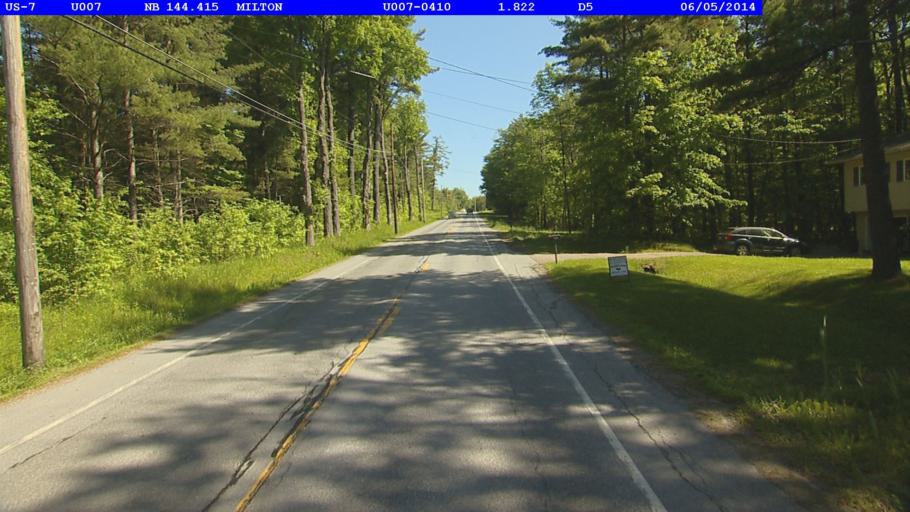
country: US
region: Vermont
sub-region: Chittenden County
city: Milton
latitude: 44.6193
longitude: -73.1491
